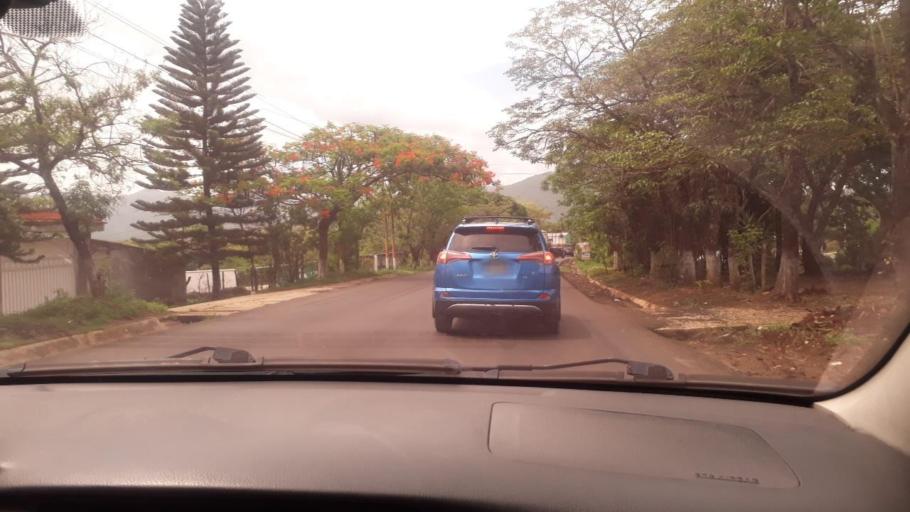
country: GT
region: Jutiapa
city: Quesada
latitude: 14.2569
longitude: -90.0248
